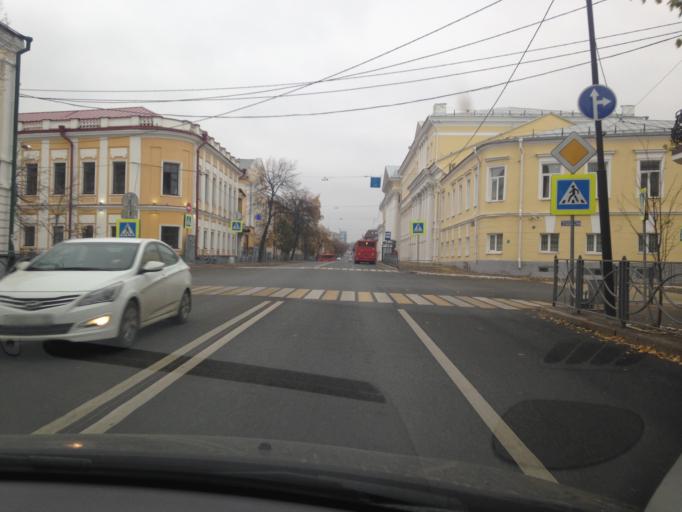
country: RU
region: Tatarstan
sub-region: Gorod Kazan'
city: Kazan
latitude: 55.7974
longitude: 49.1119
